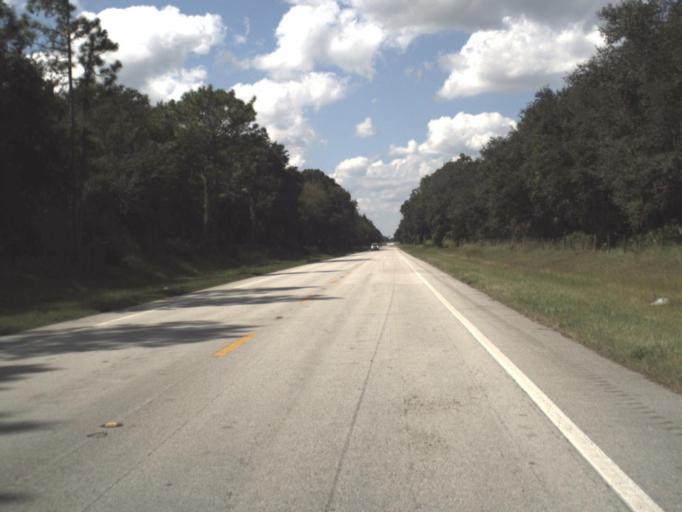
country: US
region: Florida
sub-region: Highlands County
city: Sebring
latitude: 27.4124
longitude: -81.5393
